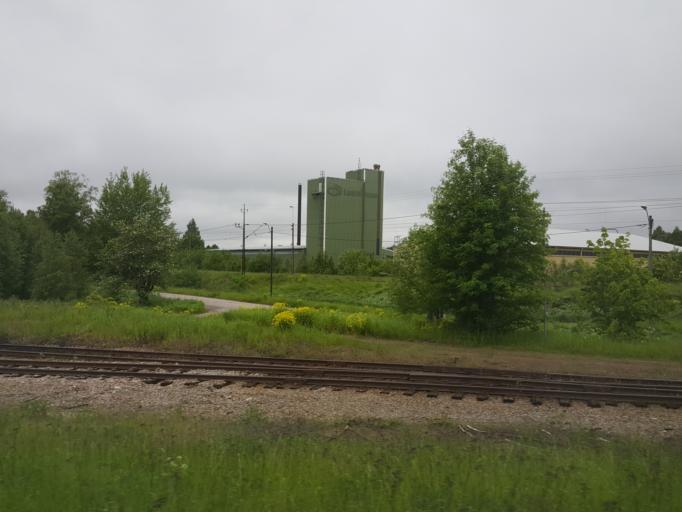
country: SE
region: Dalarna
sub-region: Avesta Kommun
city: Avesta
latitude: 60.1244
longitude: 16.2196
